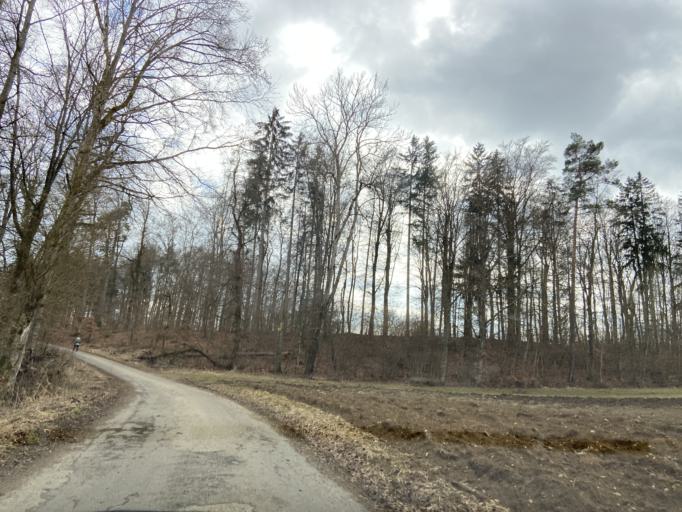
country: DE
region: Baden-Wuerttemberg
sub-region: Tuebingen Region
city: Bingen
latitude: 48.1187
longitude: 9.2576
